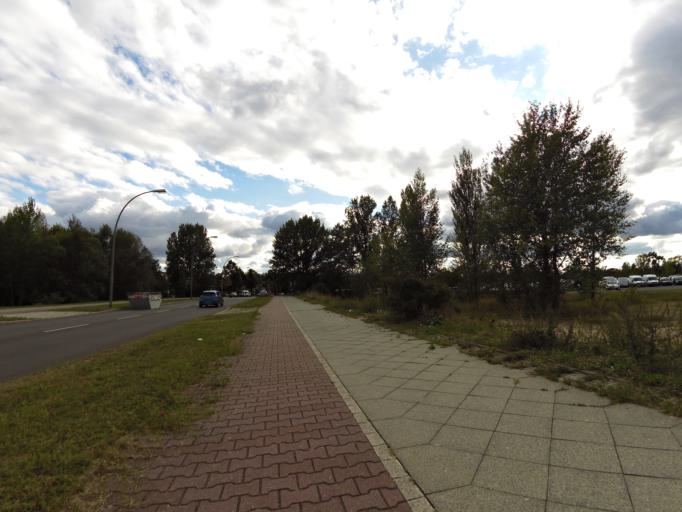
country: DE
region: Berlin
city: Altglienicke
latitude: 52.4232
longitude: 13.5192
